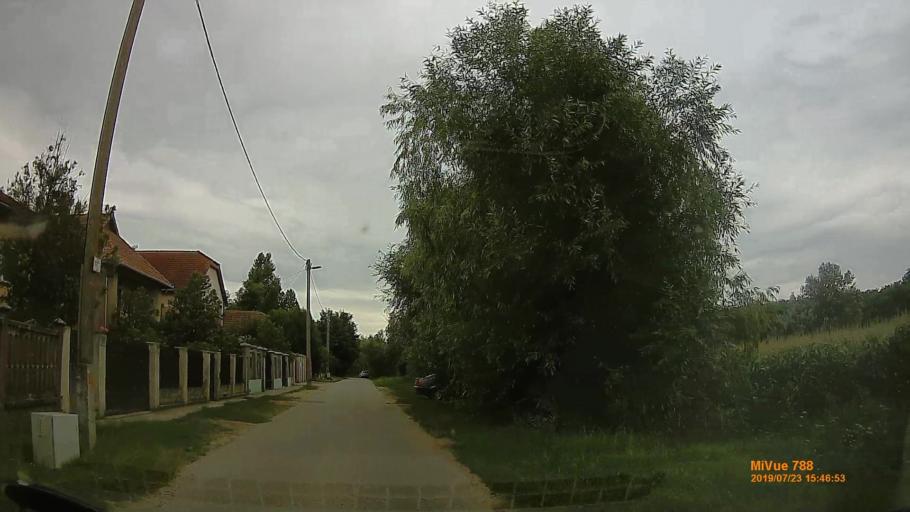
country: HU
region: Szabolcs-Szatmar-Bereg
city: Kotaj
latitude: 48.0214
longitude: 21.6880
